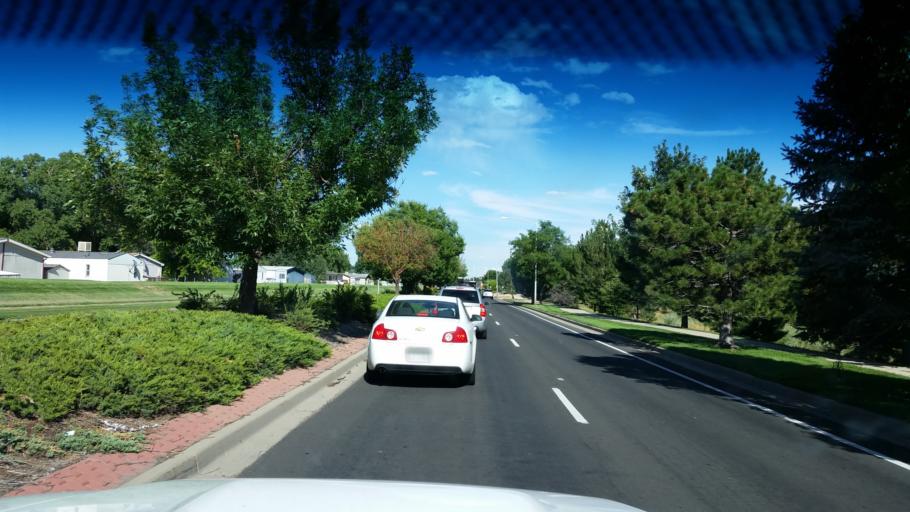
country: US
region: Colorado
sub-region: Adams County
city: Northglenn
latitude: 39.9285
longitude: -105.0210
